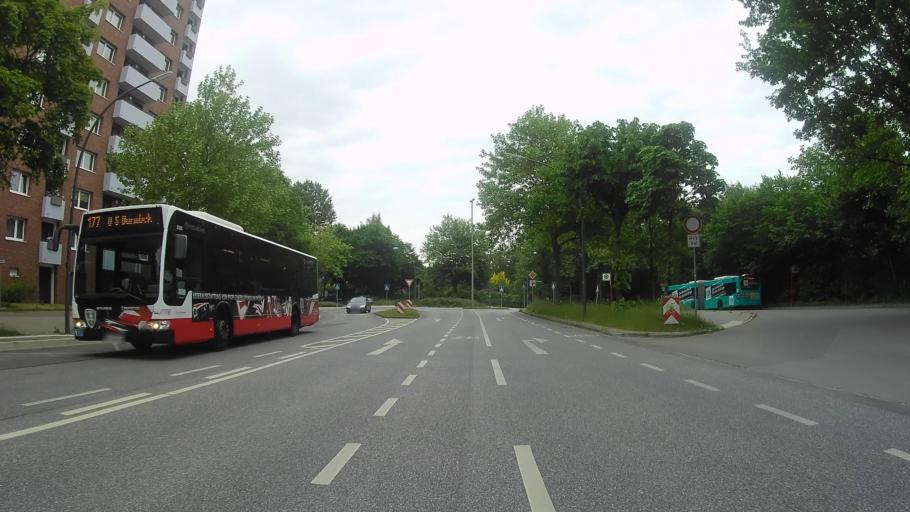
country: DE
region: Hamburg
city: Steilshoop
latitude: 53.6147
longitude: 10.0687
